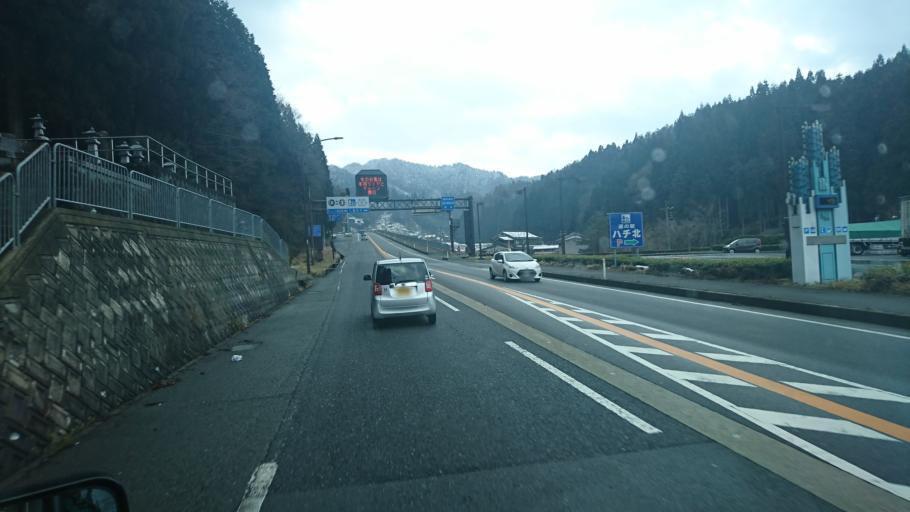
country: JP
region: Hyogo
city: Toyooka
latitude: 35.4117
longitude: 134.6006
